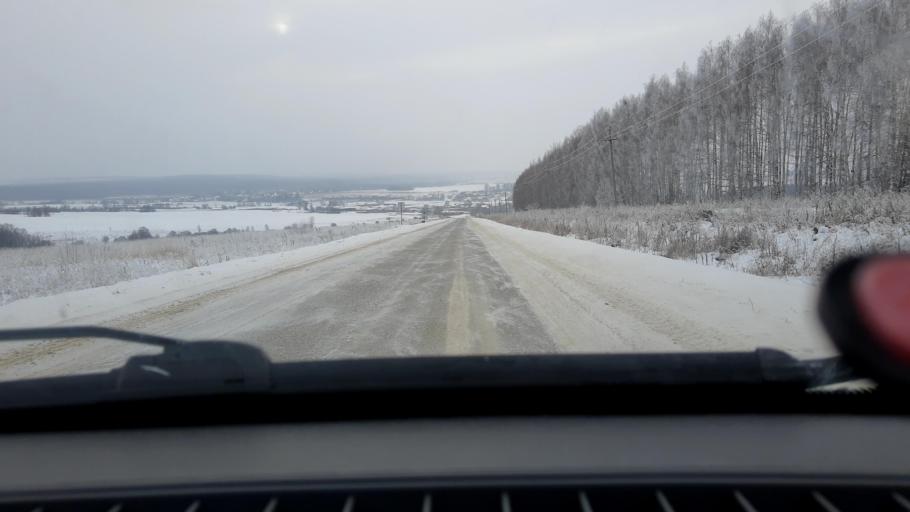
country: RU
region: Bashkortostan
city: Iglino
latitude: 54.6553
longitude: 56.4255
